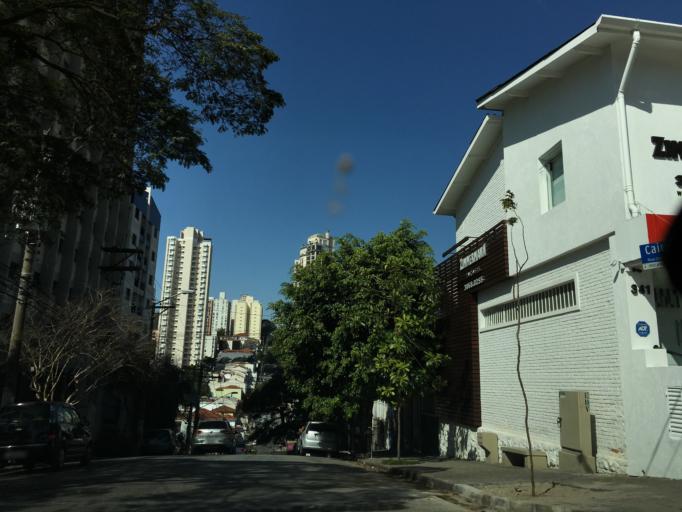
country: BR
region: Sao Paulo
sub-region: Sao Paulo
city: Sao Paulo
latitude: -23.5375
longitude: -46.6761
